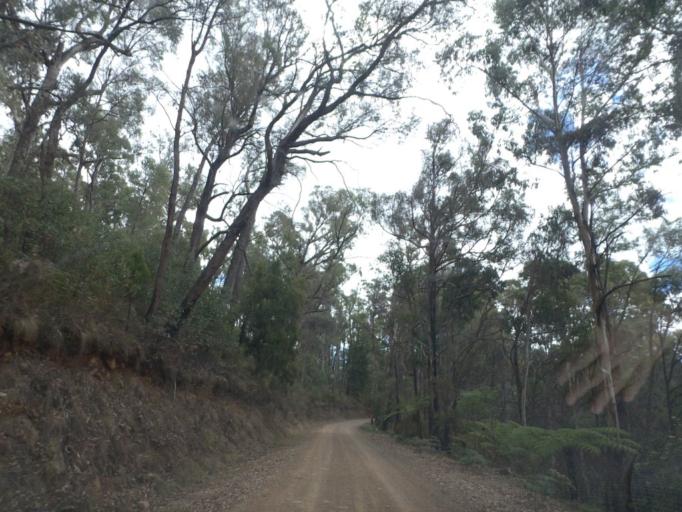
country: AU
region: Victoria
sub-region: Murrindindi
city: Alexandra
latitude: -37.4282
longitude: 145.9758
